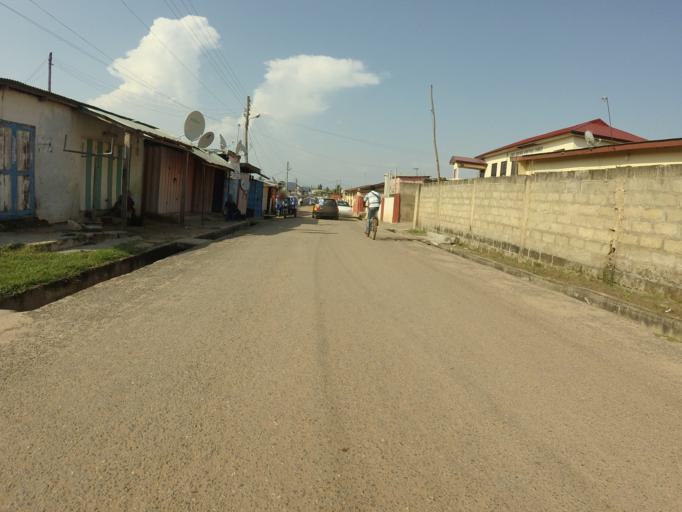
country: GH
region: Greater Accra
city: Dome
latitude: 5.6119
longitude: -0.2439
